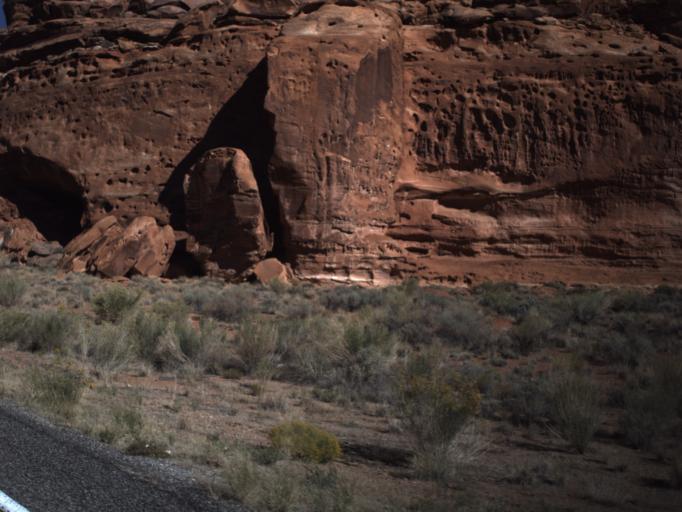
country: US
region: Utah
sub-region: San Juan County
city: Blanding
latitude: 37.9882
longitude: -110.4940
